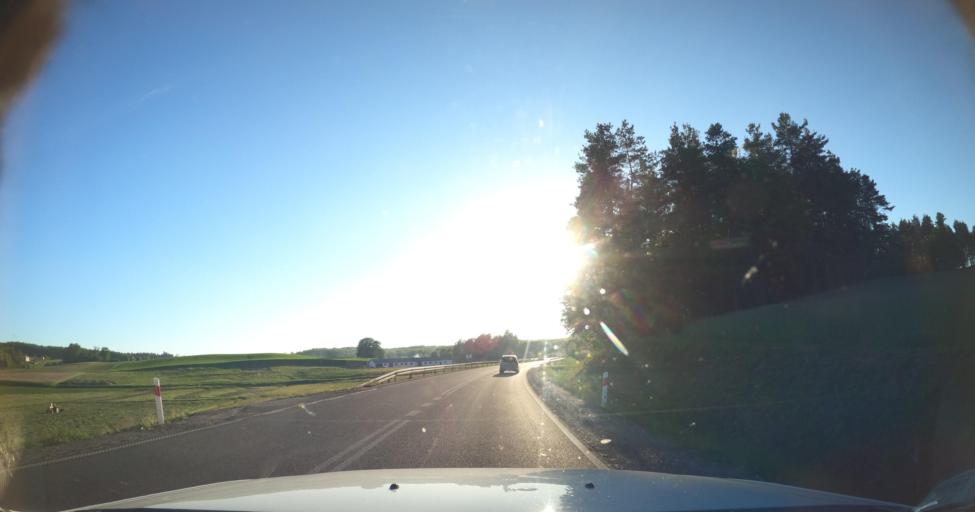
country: PL
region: Pomeranian Voivodeship
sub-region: Powiat kartuski
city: Chmielno
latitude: 54.3428
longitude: 18.0097
